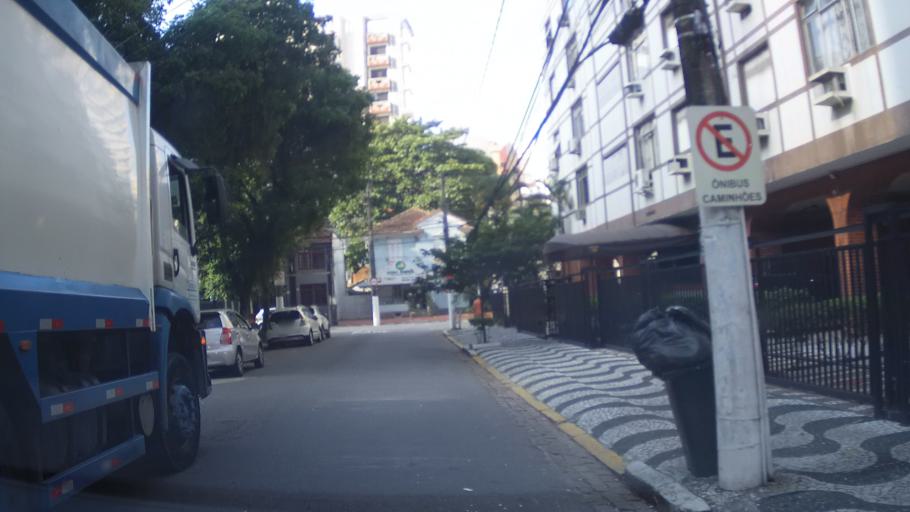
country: BR
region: Sao Paulo
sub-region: Santos
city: Santos
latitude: -23.9658
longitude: -46.3278
